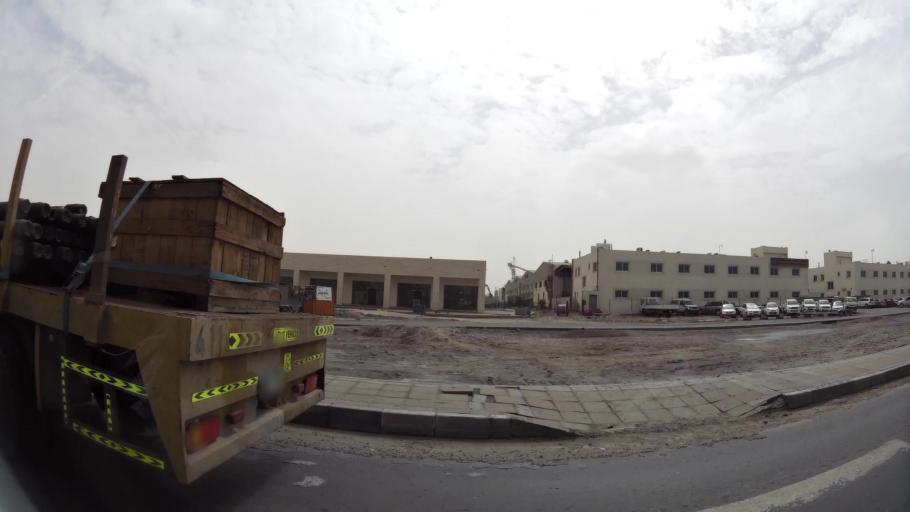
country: AE
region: Abu Dhabi
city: Abu Dhabi
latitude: 24.3461
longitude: 54.5113
